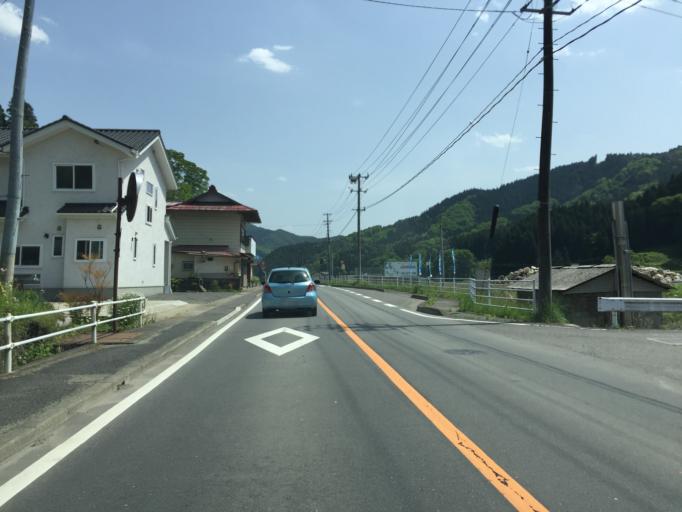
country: JP
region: Fukushima
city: Ishikawa
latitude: 37.0921
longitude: 140.5147
